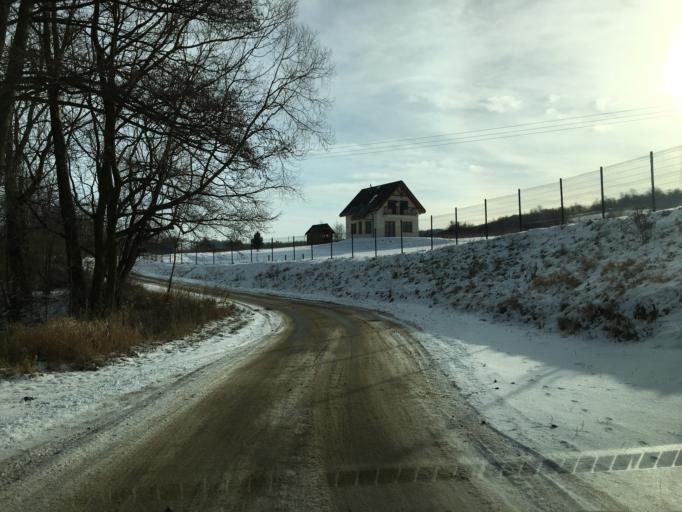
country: PL
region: Lower Silesian Voivodeship
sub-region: Powiat walbrzyski
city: Gluszyca Gorna
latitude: 50.6741
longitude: 16.3640
